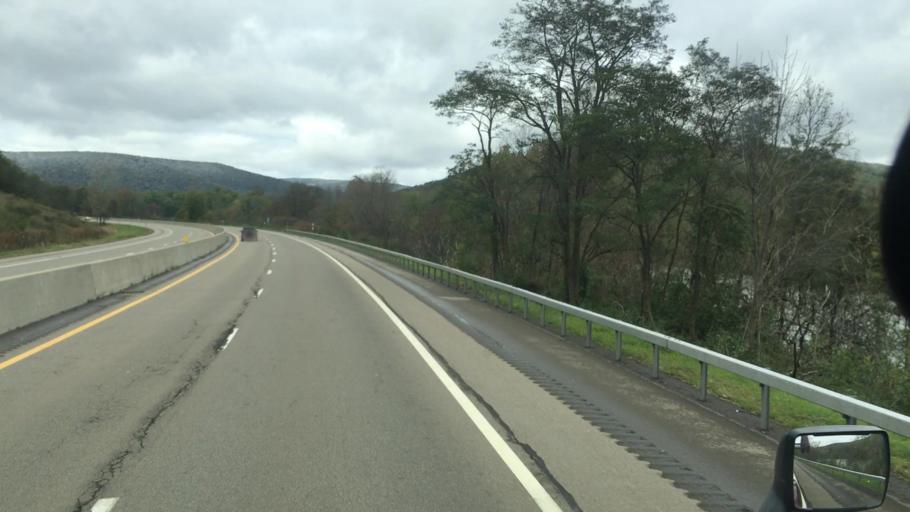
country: US
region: New York
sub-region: Cattaraugus County
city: Salamanca
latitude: 42.1434
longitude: -78.6677
